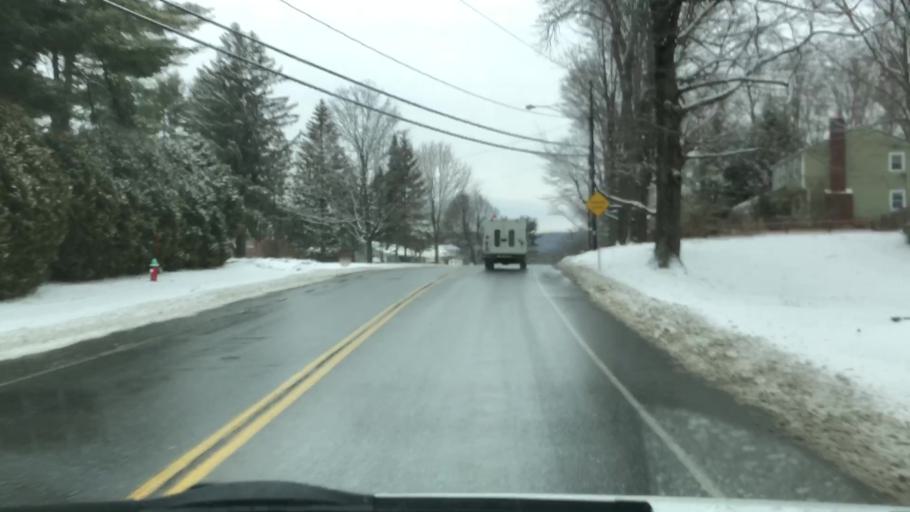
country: US
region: Massachusetts
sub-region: Berkshire County
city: Dalton
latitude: 42.4610
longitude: -73.1817
